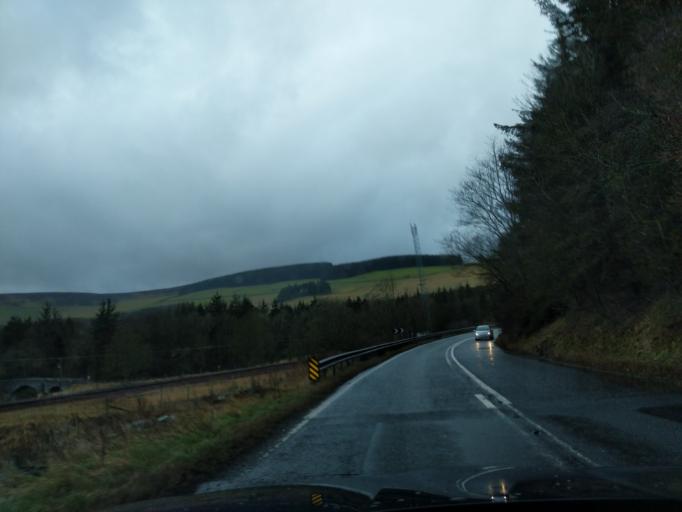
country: GB
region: Scotland
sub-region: The Scottish Borders
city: Galashiels
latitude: 55.6650
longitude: -2.8762
